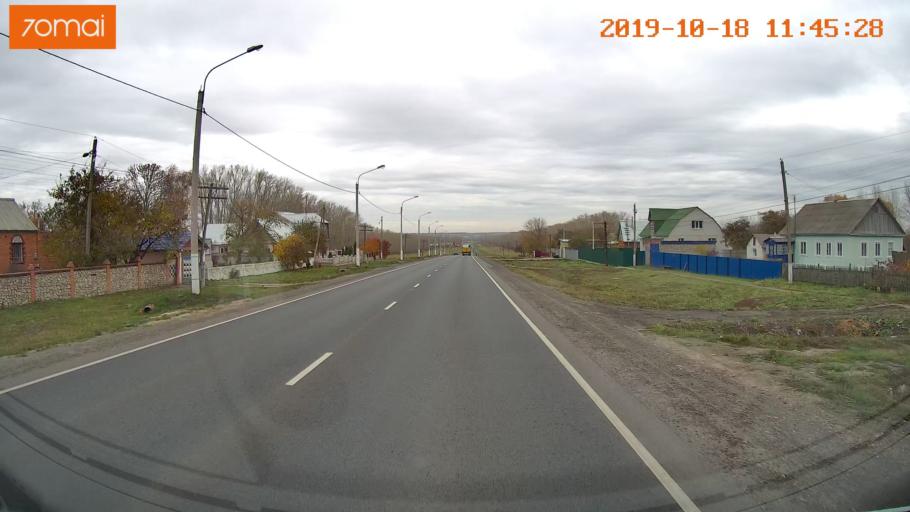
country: RU
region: Rjazan
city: Mikhaylov
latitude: 54.2107
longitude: 38.9704
